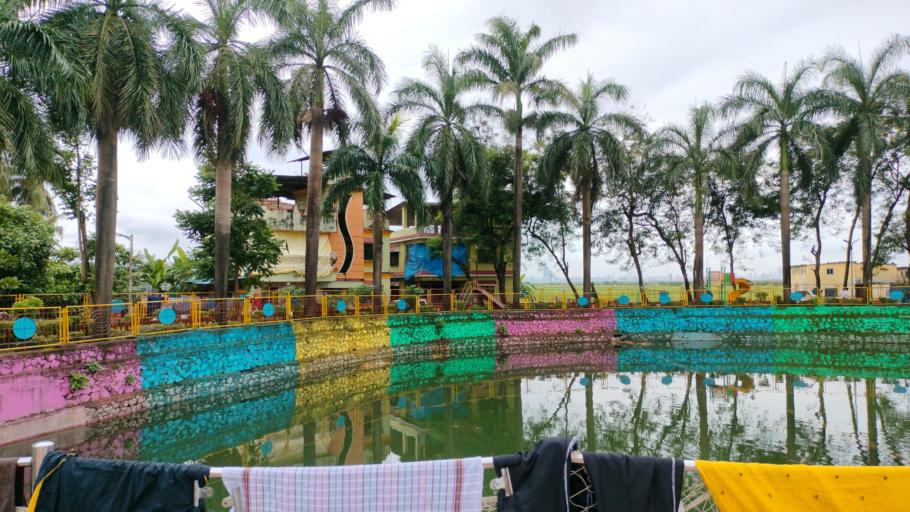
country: IN
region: Maharashtra
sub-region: Thane
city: Bhayandar
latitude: 19.2933
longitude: 72.8205
